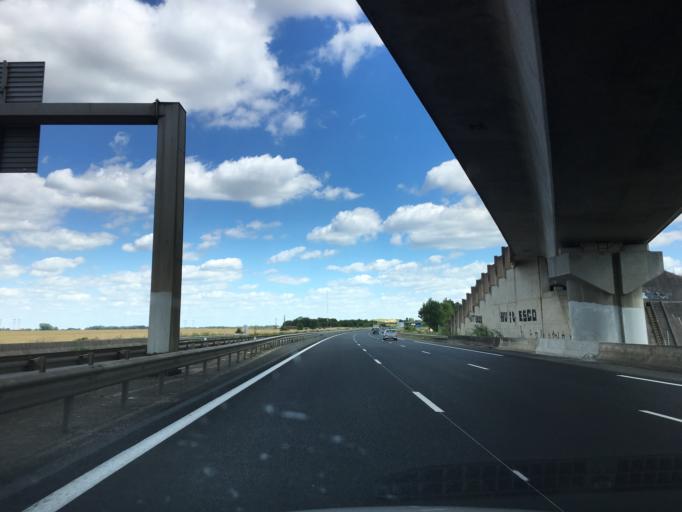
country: FR
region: Ile-de-France
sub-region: Departement de Seine-et-Marne
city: Moisenay
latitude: 48.5839
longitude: 2.7312
